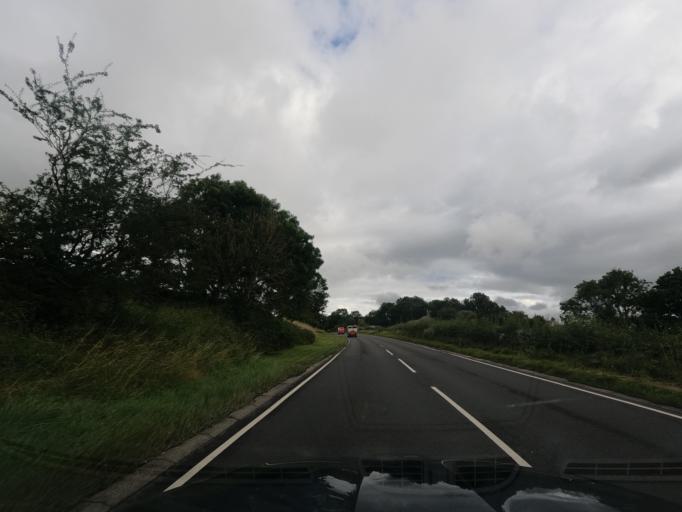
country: GB
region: England
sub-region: Northumberland
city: Wooler
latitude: 55.4885
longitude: -1.9420
